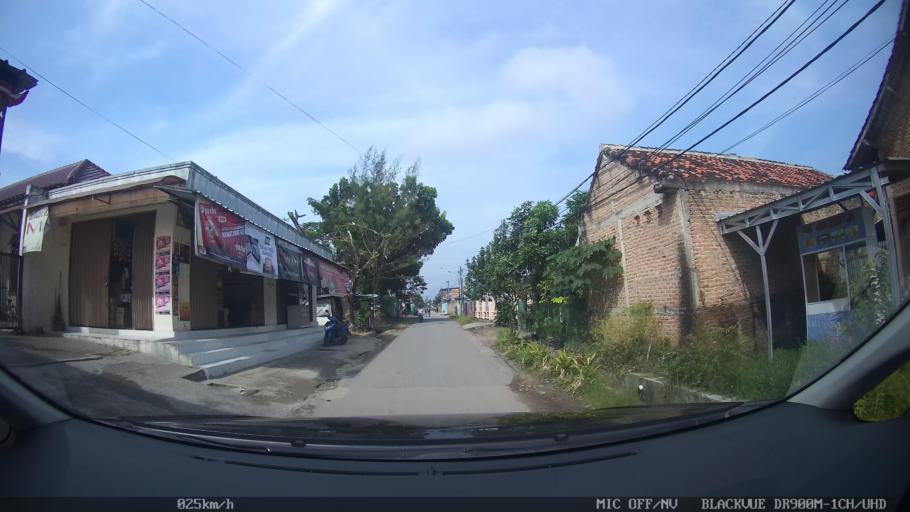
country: ID
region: Lampung
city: Kedaton
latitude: -5.3811
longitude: 105.2973
